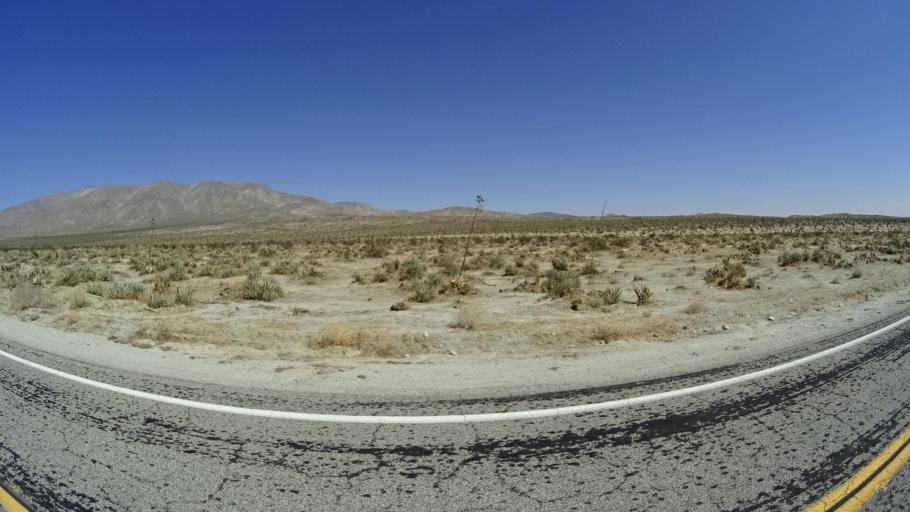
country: US
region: California
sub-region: San Diego County
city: Pine Valley
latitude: 32.9473
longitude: -116.2803
